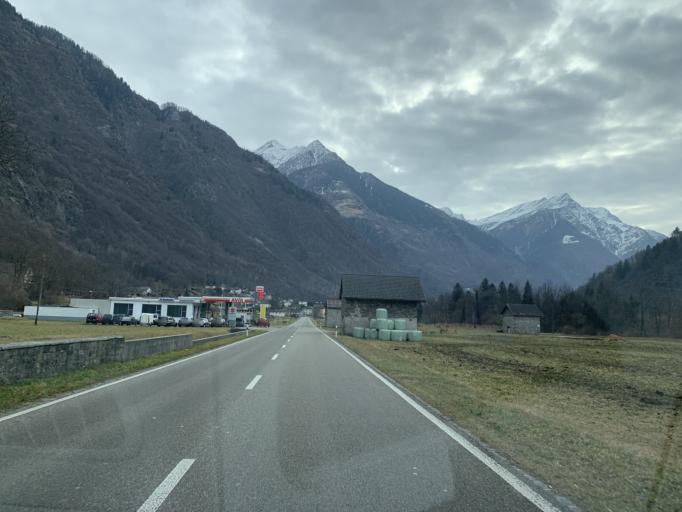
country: CH
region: Ticino
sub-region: Blenio District
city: Malvaglia
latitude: 46.4318
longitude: 8.9649
